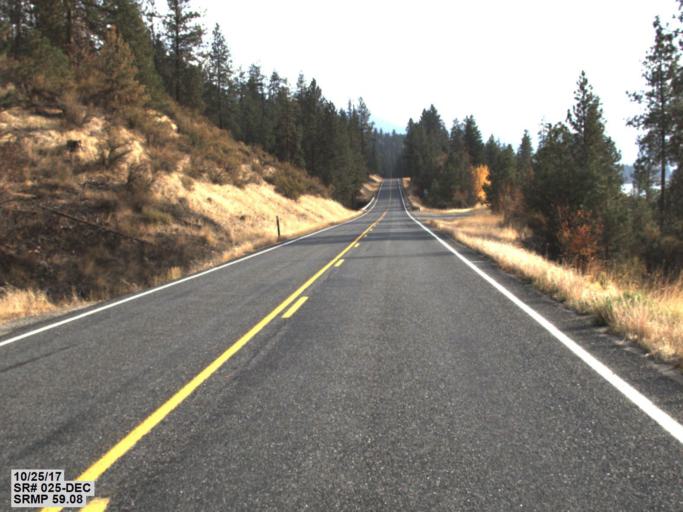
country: US
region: Washington
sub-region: Stevens County
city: Kettle Falls
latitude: 48.3256
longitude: -118.1524
